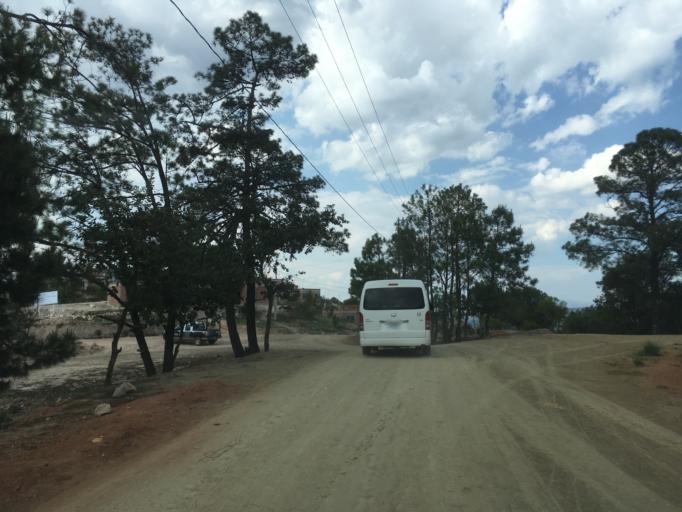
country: MX
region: Oaxaca
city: Santiago Tilantongo
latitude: 17.2194
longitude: -97.2711
